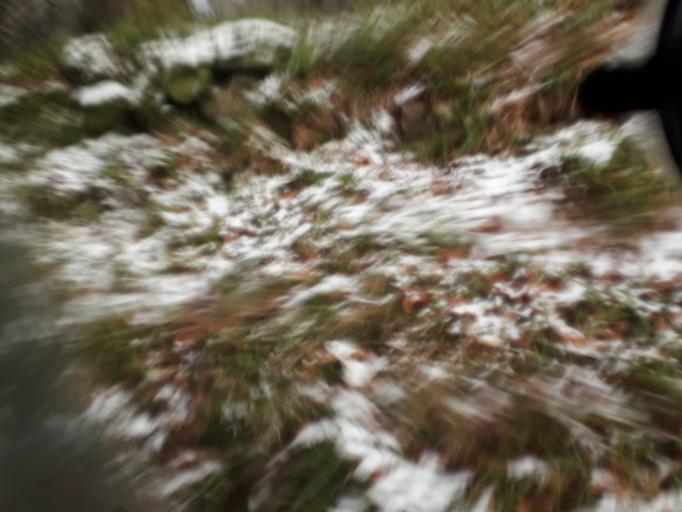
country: IE
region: Leinster
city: Ballyboden
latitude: 53.2393
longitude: -6.3143
